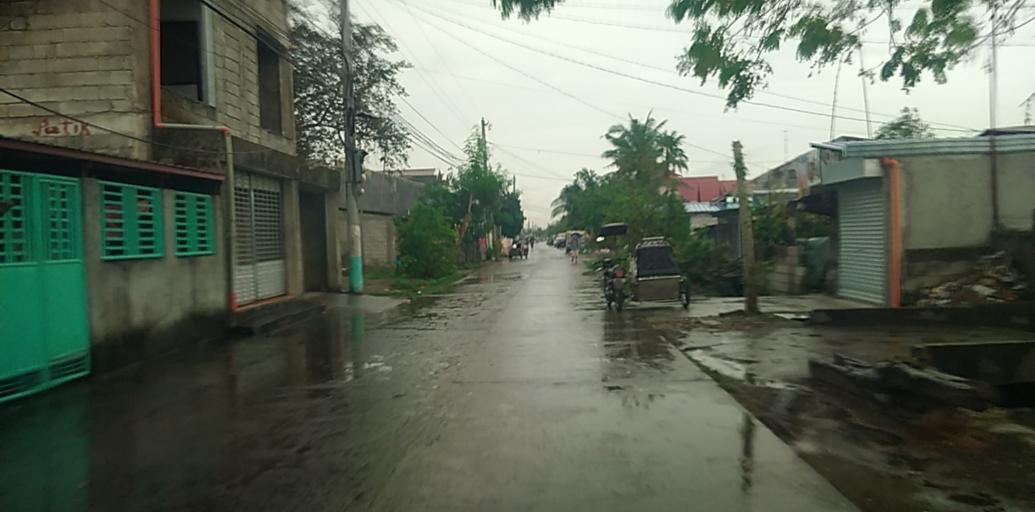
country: PH
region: Central Luzon
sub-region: Province of Pampanga
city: Arenas
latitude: 15.1643
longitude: 120.6901
